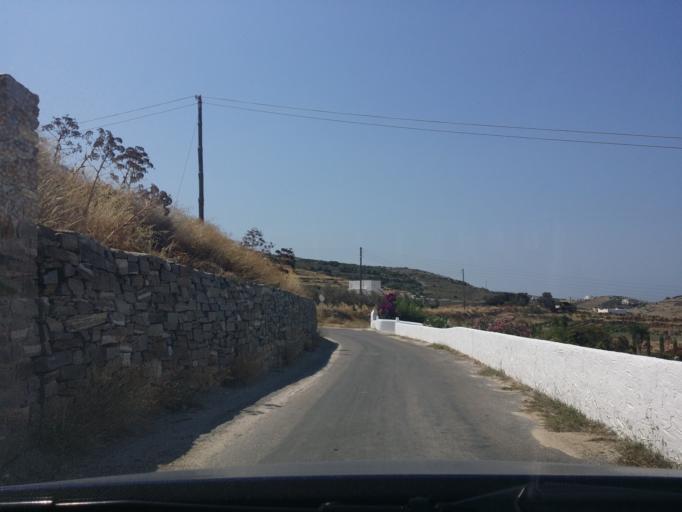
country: GR
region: South Aegean
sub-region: Nomos Kykladon
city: Antiparos
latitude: 37.0465
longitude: 25.1255
